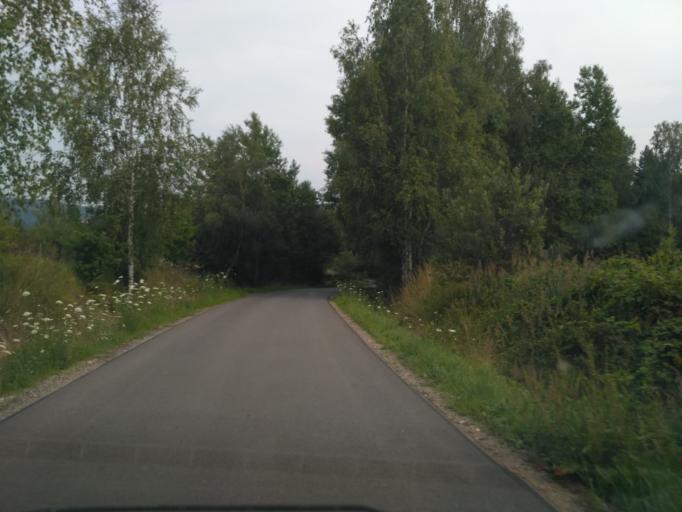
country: PL
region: Subcarpathian Voivodeship
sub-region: Powiat strzyzowski
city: Jawornik
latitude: 49.8560
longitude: 21.8924
